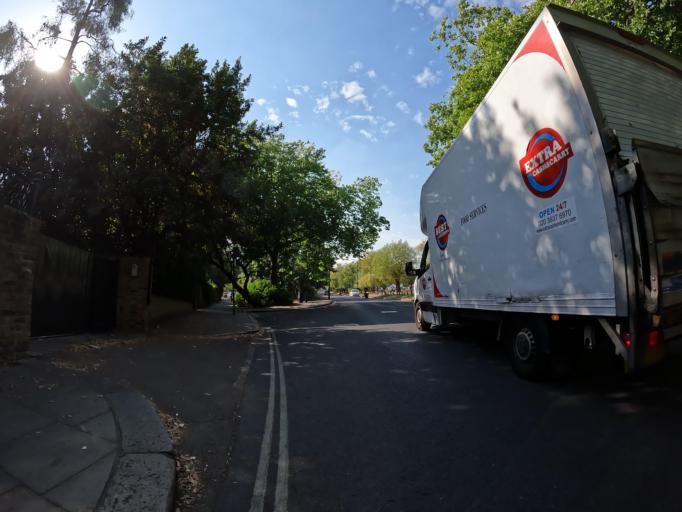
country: GB
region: England
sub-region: Greater London
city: Hadley Wood
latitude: 51.6601
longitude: -0.1736
